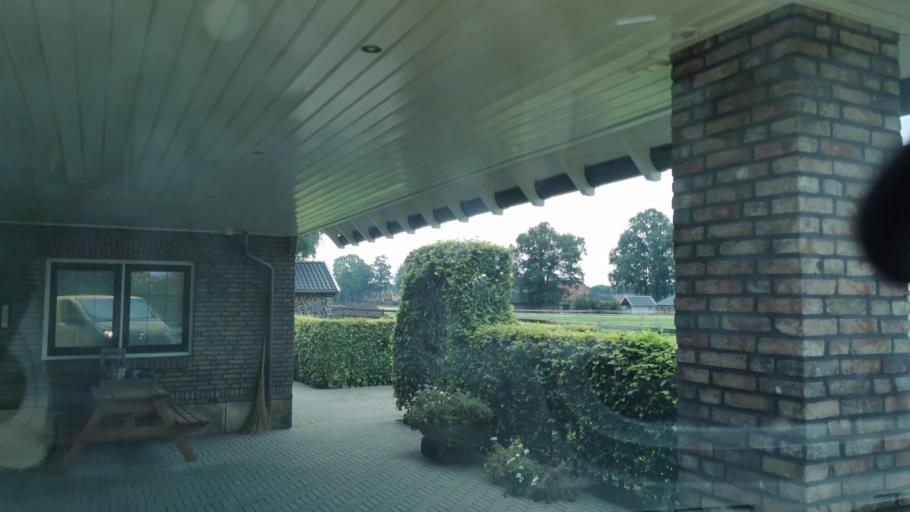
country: NL
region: Overijssel
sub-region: Gemeente Oldenzaal
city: Oldenzaal
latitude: 52.3582
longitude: 6.8635
